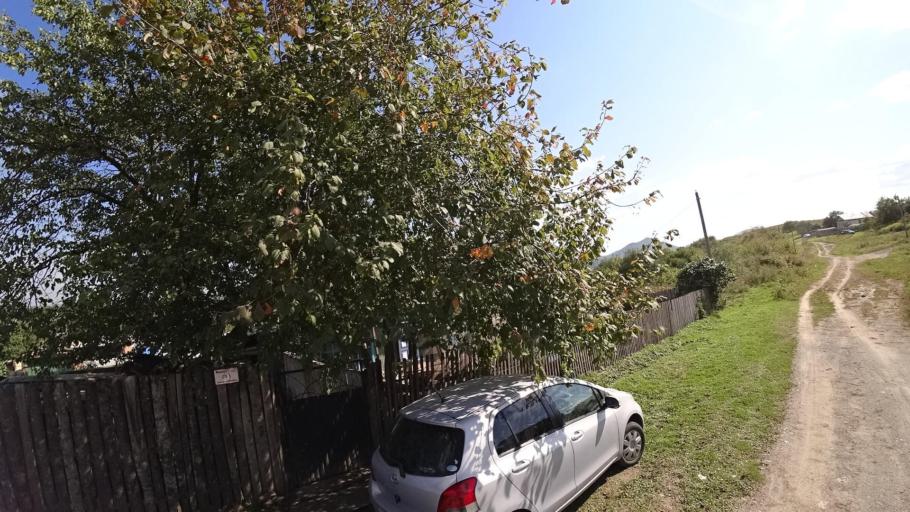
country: RU
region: Jewish Autonomous Oblast
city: Londoko
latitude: 49.0108
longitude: 131.8664
